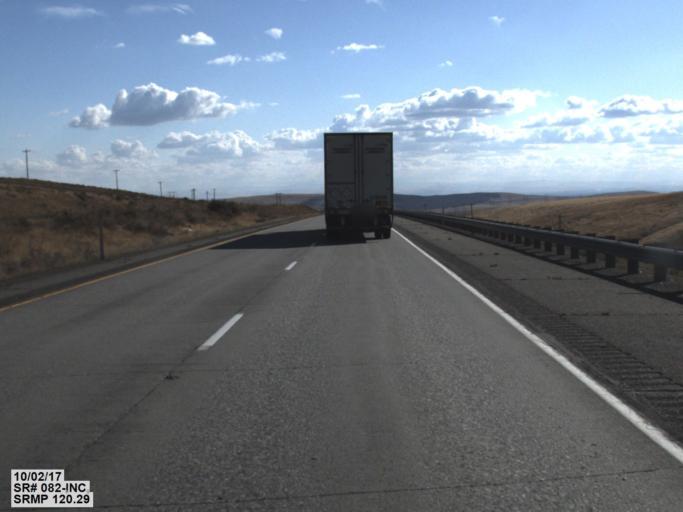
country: US
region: Washington
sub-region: Benton County
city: Highland
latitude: 46.0610
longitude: -119.2238
